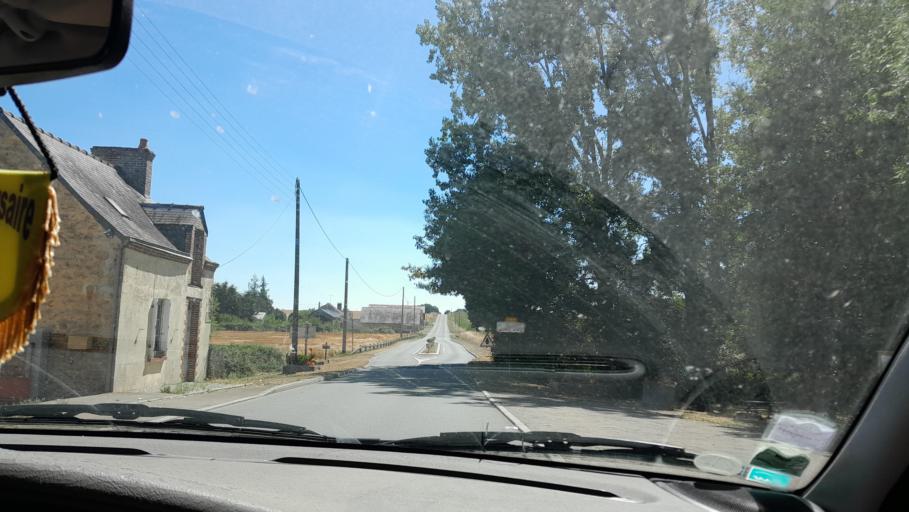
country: FR
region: Pays de la Loire
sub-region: Departement de la Mayenne
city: Congrier
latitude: 47.8775
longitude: -1.1284
